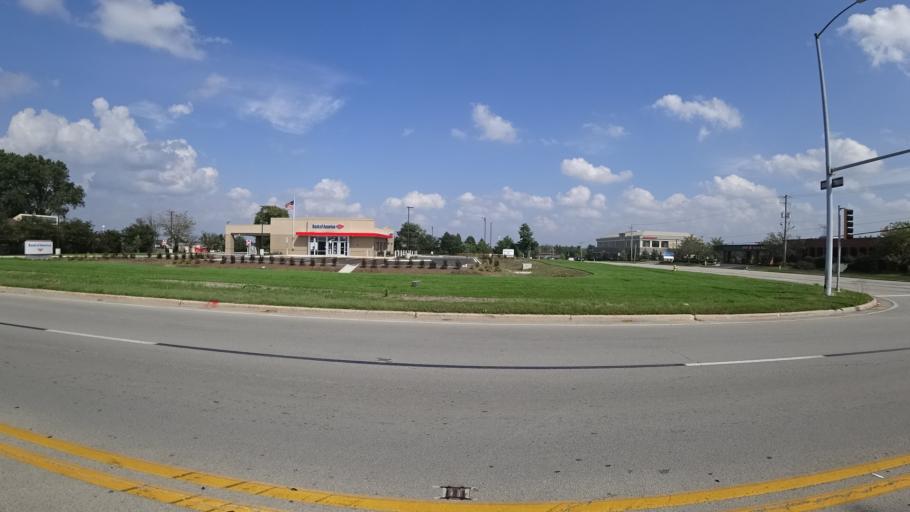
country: US
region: Illinois
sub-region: Will County
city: Goodings Grove
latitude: 41.6295
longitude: -87.9311
